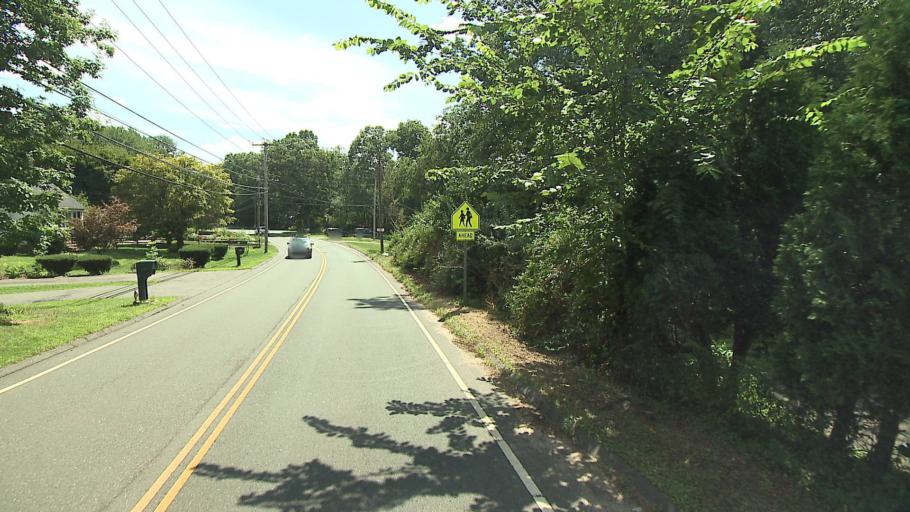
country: US
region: Connecticut
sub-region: Fairfield County
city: Trumbull
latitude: 41.2630
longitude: -73.1673
